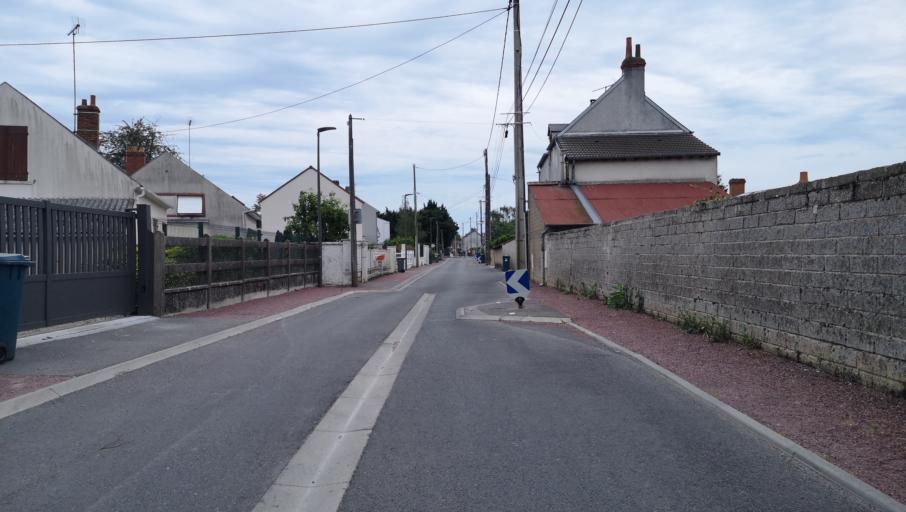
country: FR
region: Centre
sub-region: Departement du Loiret
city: Saint-Pryve-Saint-Mesmin
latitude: 47.8899
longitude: 1.8722
